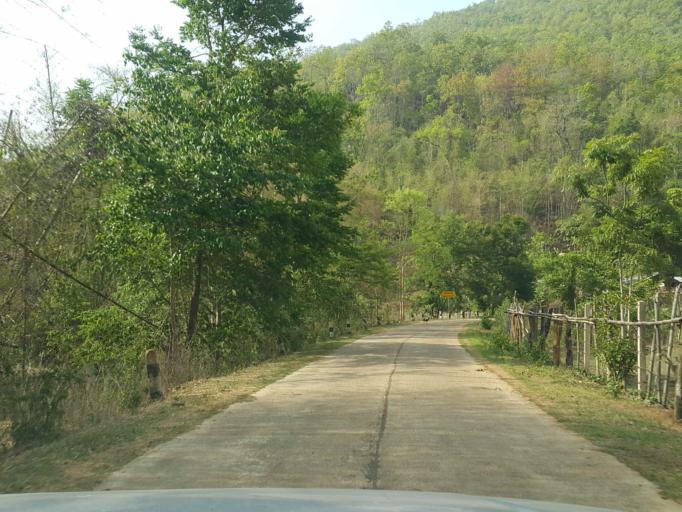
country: TH
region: Chiang Mai
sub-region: Amphoe Chiang Dao
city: Chiang Dao
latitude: 19.3995
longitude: 98.7749
